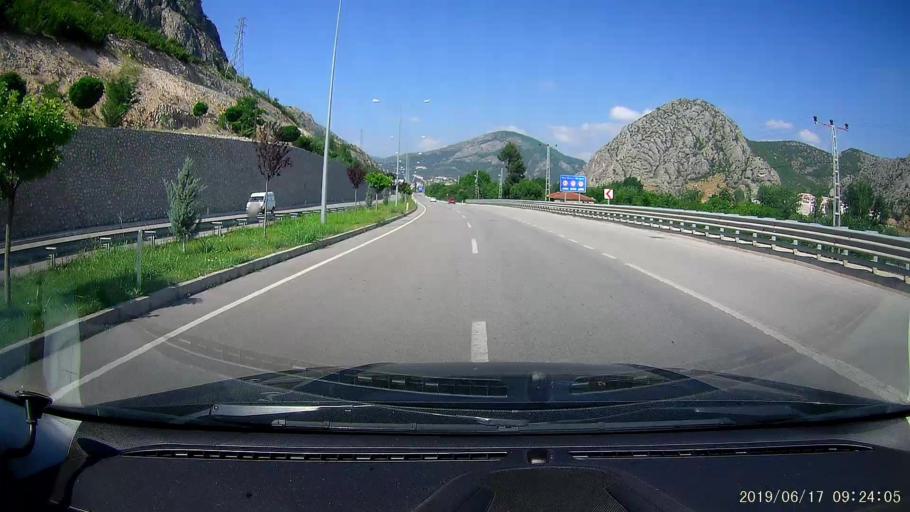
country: TR
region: Amasya
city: Amasya
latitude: 40.6737
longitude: 35.8622
